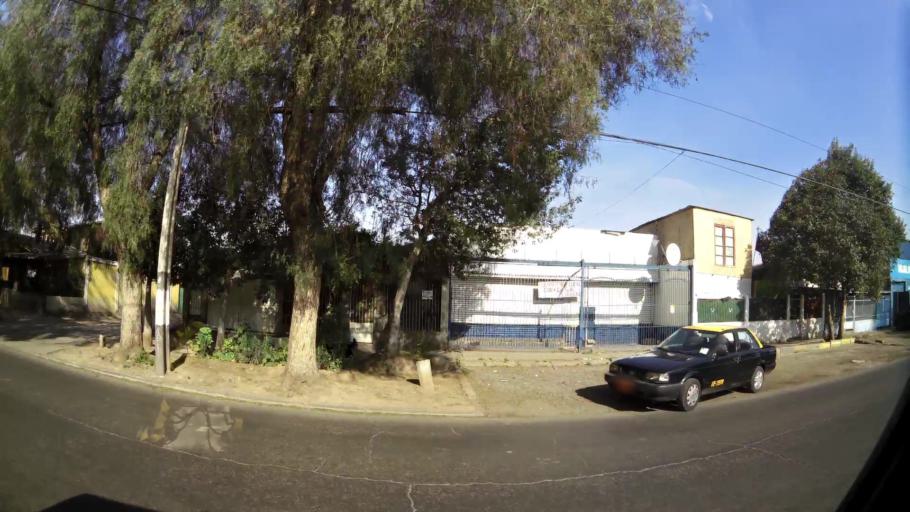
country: CL
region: Santiago Metropolitan
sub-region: Provincia de Santiago
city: Lo Prado
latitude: -33.4171
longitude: -70.7532
